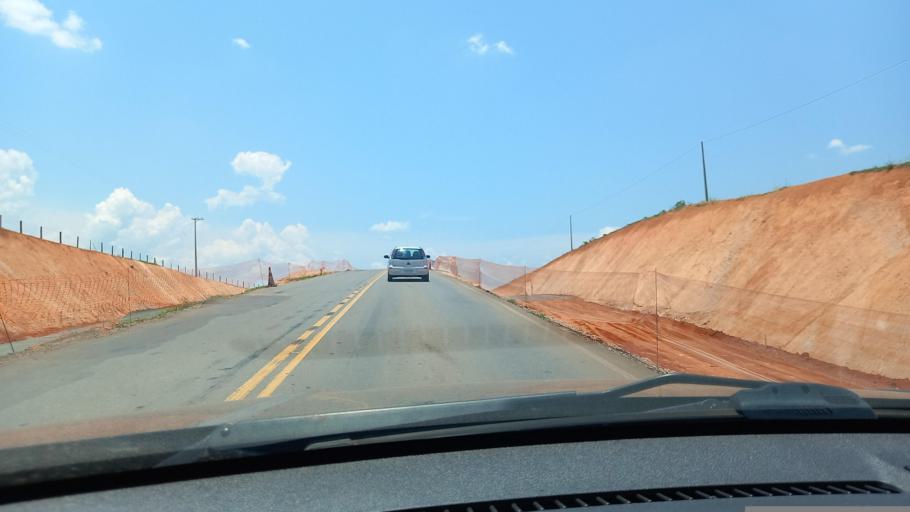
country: BR
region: Sao Paulo
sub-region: Itapira
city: Itapira
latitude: -22.3983
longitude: -46.8538
